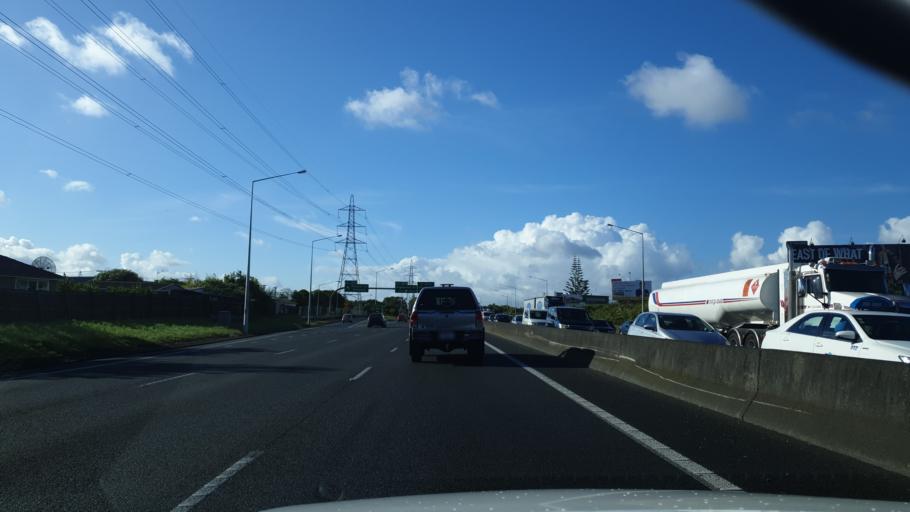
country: NZ
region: Auckland
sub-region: Auckland
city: Tamaki
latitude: -36.9342
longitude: 174.8518
